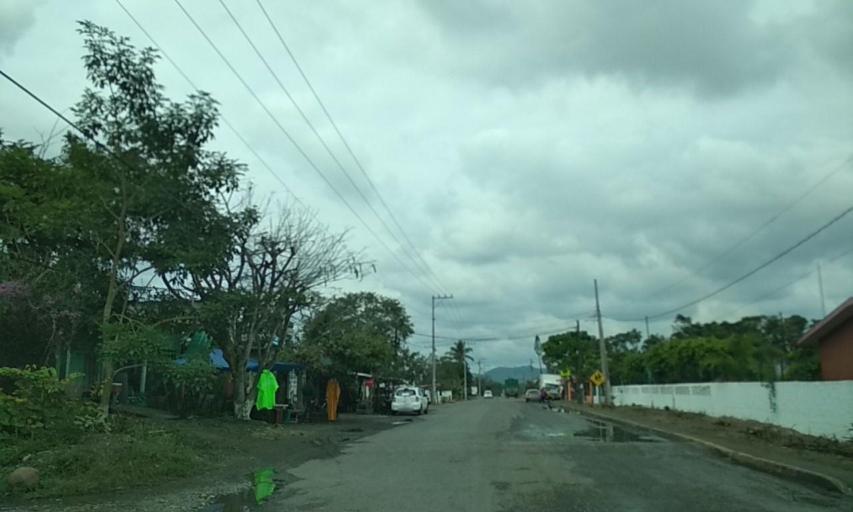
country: MX
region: Veracruz
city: Agua Dulce
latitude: 20.3626
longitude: -97.3311
